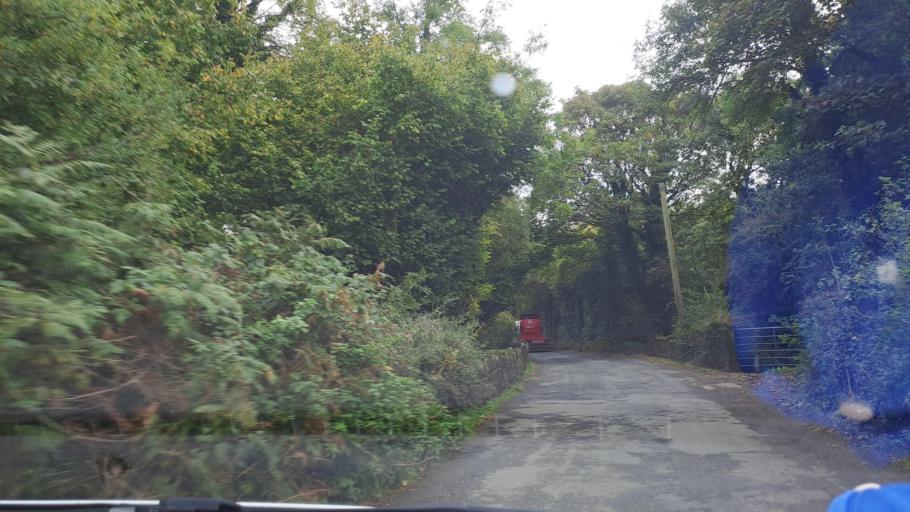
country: IE
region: Ulster
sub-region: An Cabhan
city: Kingscourt
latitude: 53.9405
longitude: -6.7909
